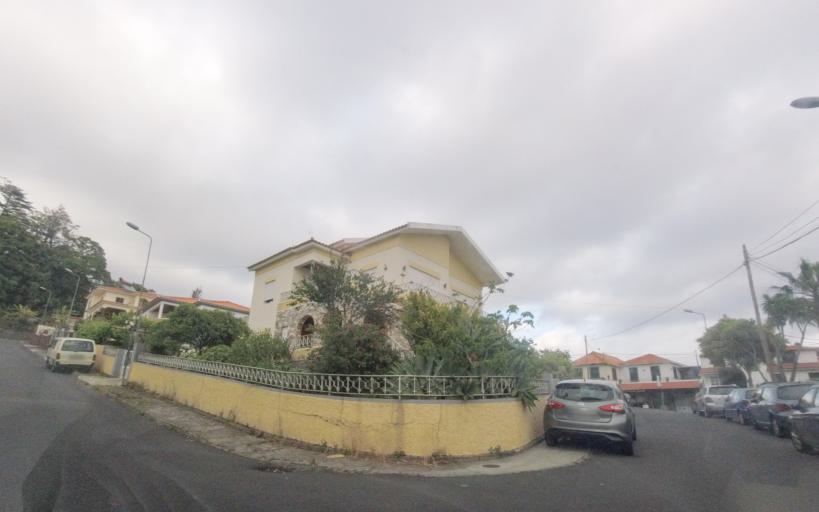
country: PT
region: Madeira
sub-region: Funchal
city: Nossa Senhora do Monte
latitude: 32.6524
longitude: -16.8916
